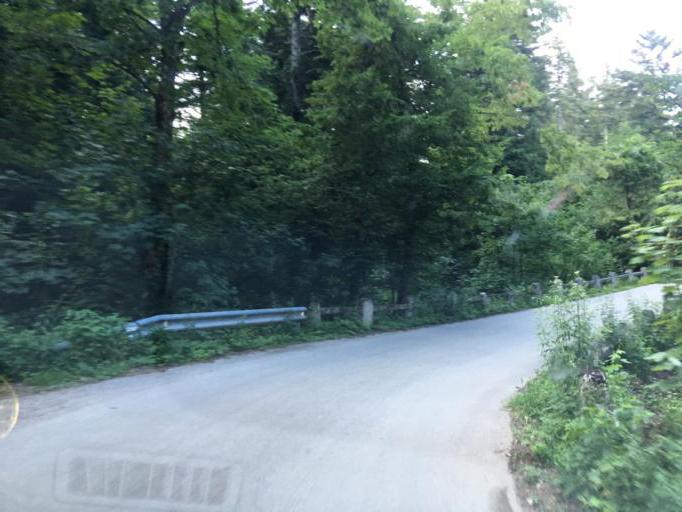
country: SI
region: Postojna
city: Postojna
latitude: 45.8003
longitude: 14.1988
